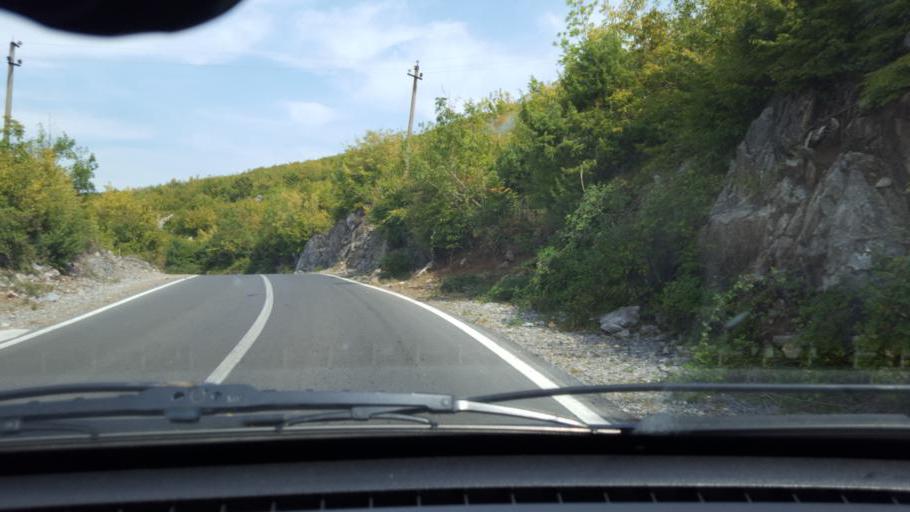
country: AL
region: Shkoder
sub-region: Rrethi i Malesia e Madhe
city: Kastrat
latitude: 42.3821
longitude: 19.4939
